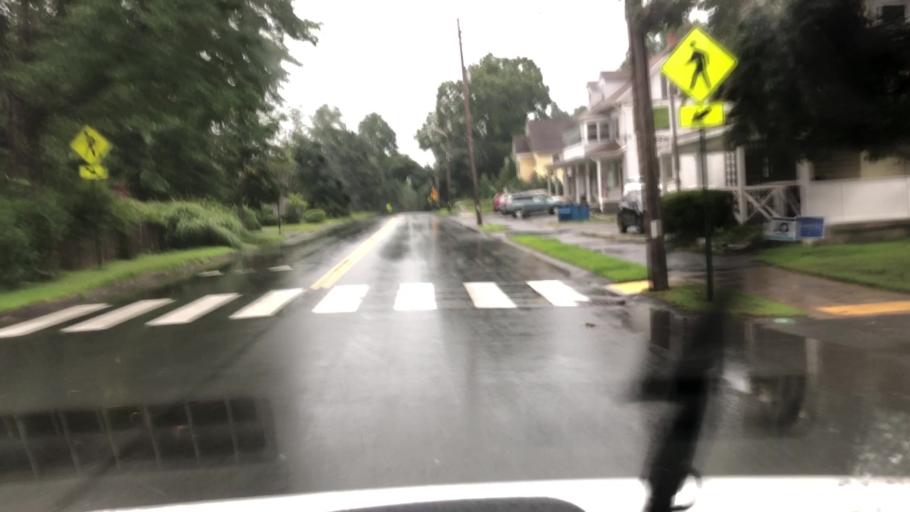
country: US
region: Massachusetts
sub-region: Hampshire County
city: Northampton
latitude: 42.3338
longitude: -72.6720
